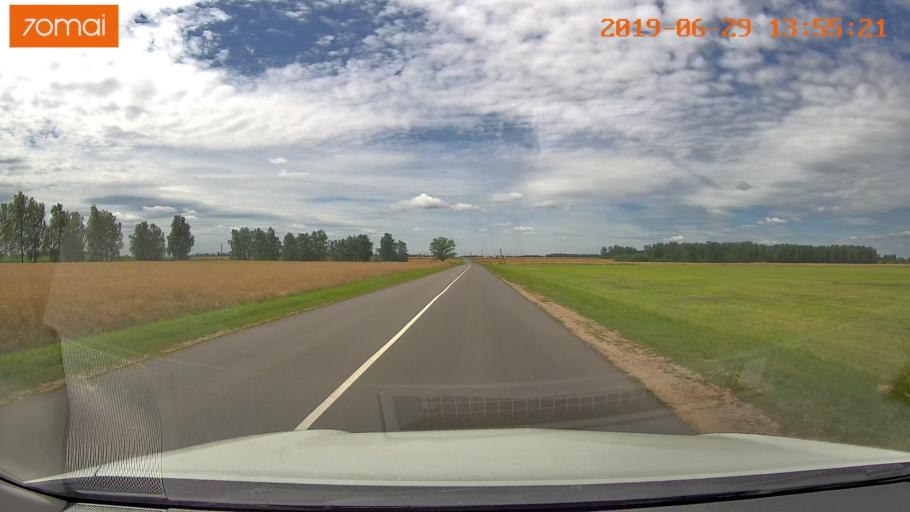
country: BY
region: Minsk
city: Slutsk
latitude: 52.9838
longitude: 27.5217
